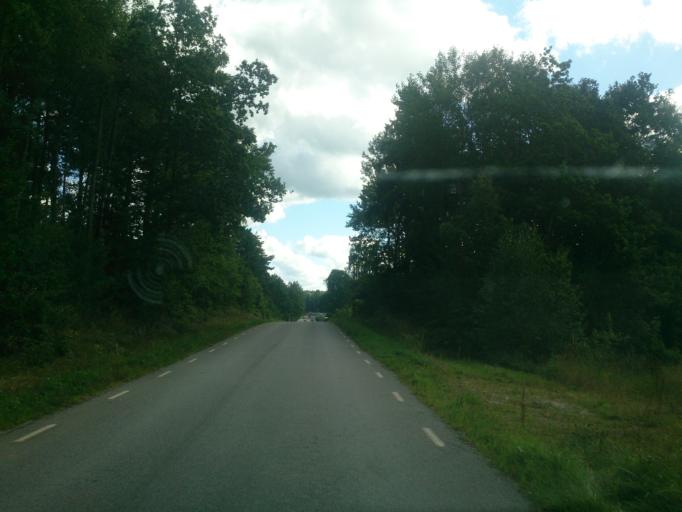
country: SE
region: OEstergoetland
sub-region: Atvidabergs Kommun
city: Atvidaberg
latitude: 58.3353
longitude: 16.0119
